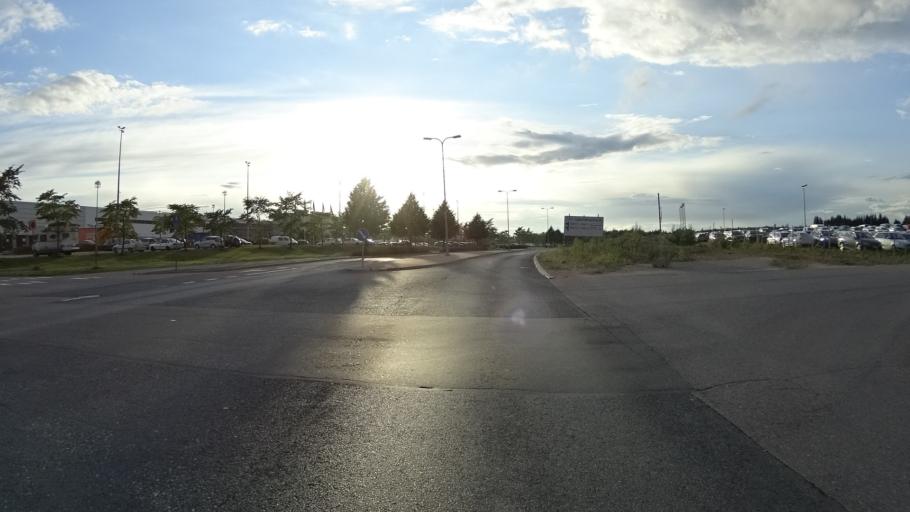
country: FI
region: Uusimaa
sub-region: Helsinki
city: Vantaa
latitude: 60.3012
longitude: 24.9282
